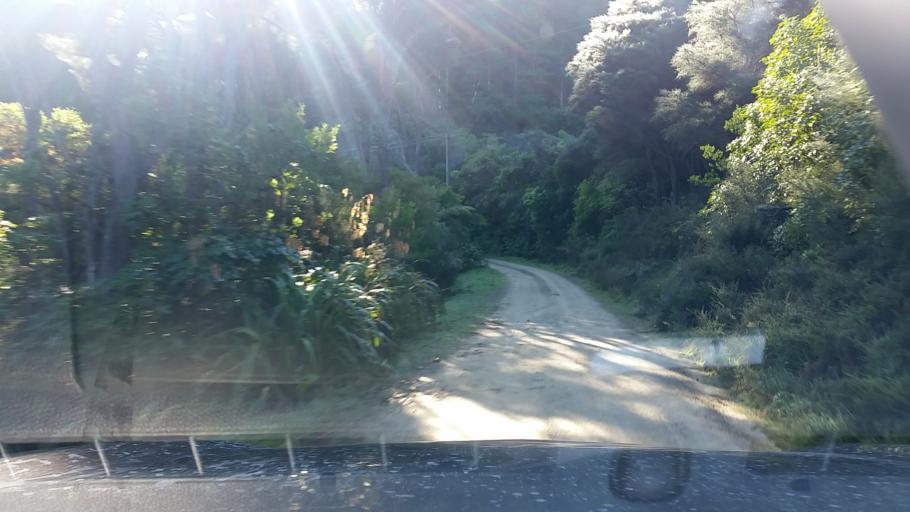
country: NZ
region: Marlborough
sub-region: Marlborough District
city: Picton
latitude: -41.1243
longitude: 173.9911
